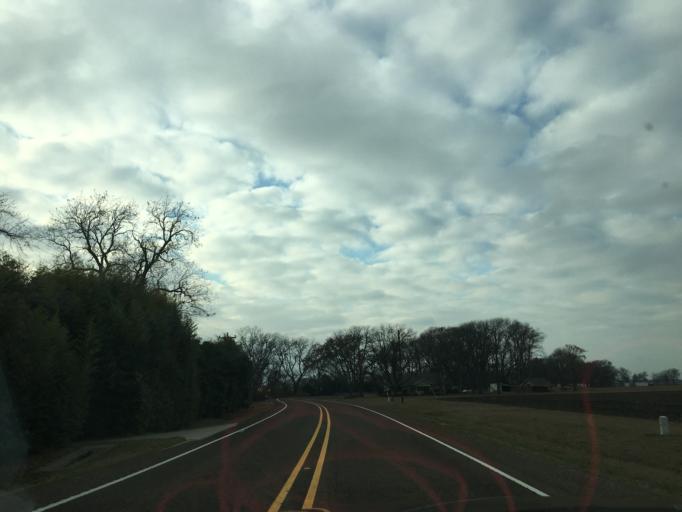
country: US
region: Texas
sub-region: Ellis County
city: Palmer
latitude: 32.4476
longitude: -96.7207
